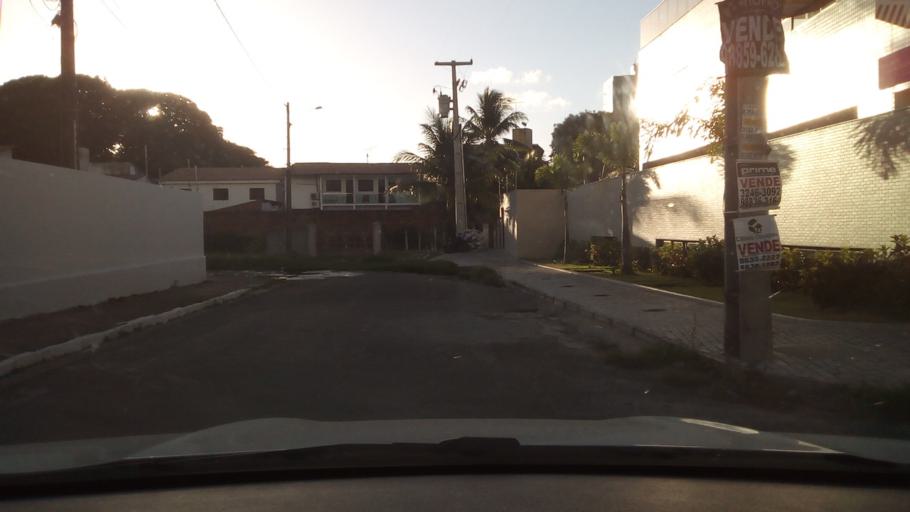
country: BR
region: Paraiba
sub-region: Joao Pessoa
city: Joao Pessoa
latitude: -7.0954
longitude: -34.8456
